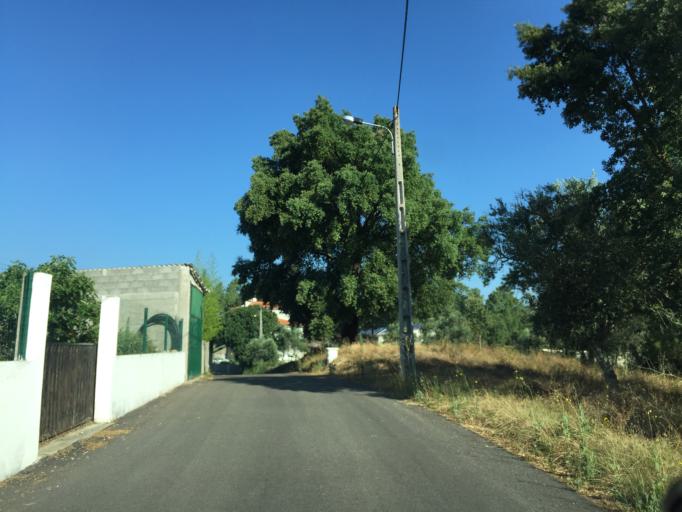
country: PT
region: Santarem
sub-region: Abrantes
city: Alferrarede
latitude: 39.5208
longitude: -8.1339
